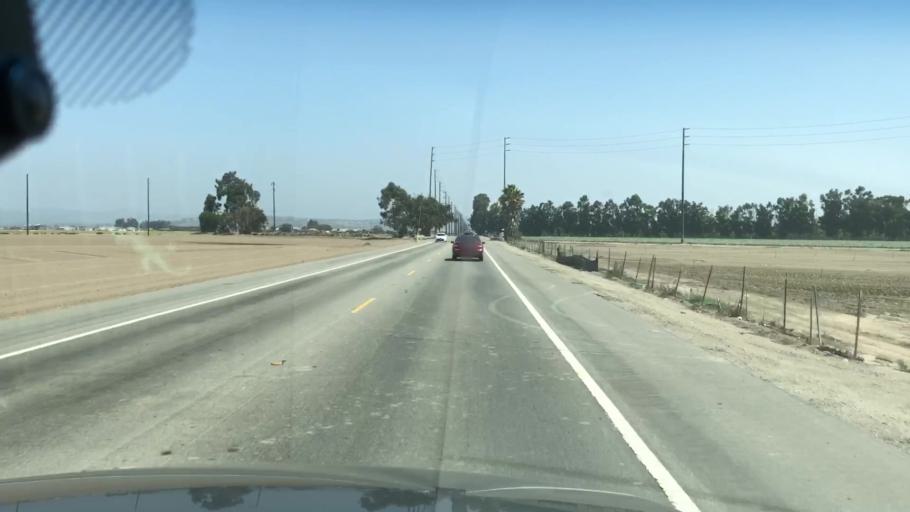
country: US
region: California
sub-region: Ventura County
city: Oxnard
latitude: 34.1795
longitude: -119.1204
